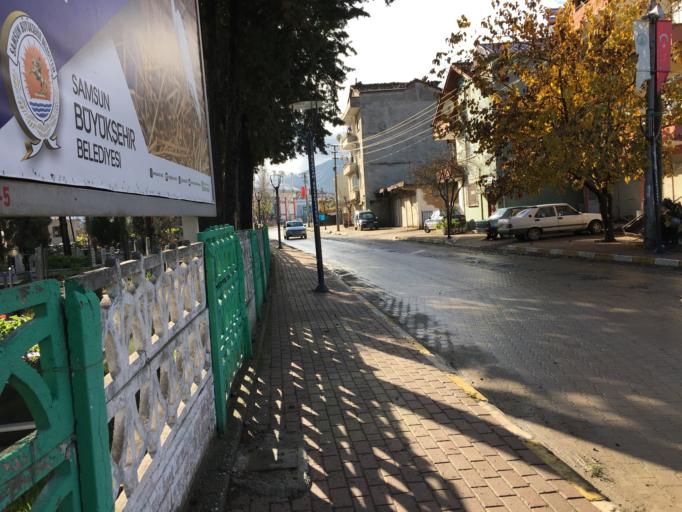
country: TR
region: Samsun
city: Alacam
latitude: 41.6146
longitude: 35.6028
